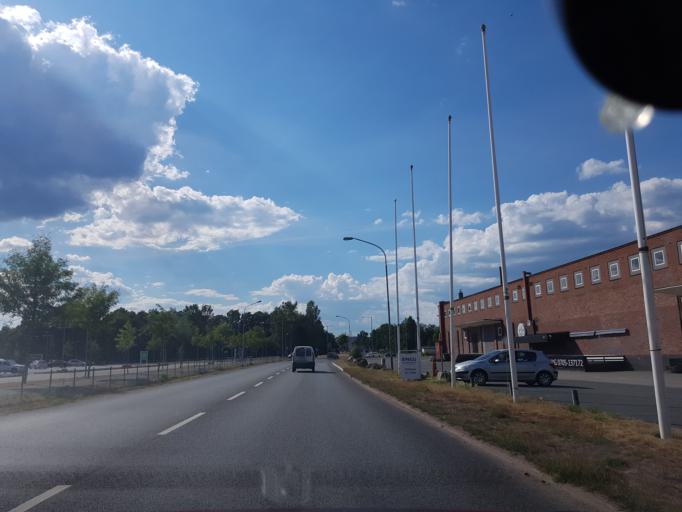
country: SE
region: Joenkoeping
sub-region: Gislaveds Kommun
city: Gislaved
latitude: 57.2991
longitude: 13.5544
